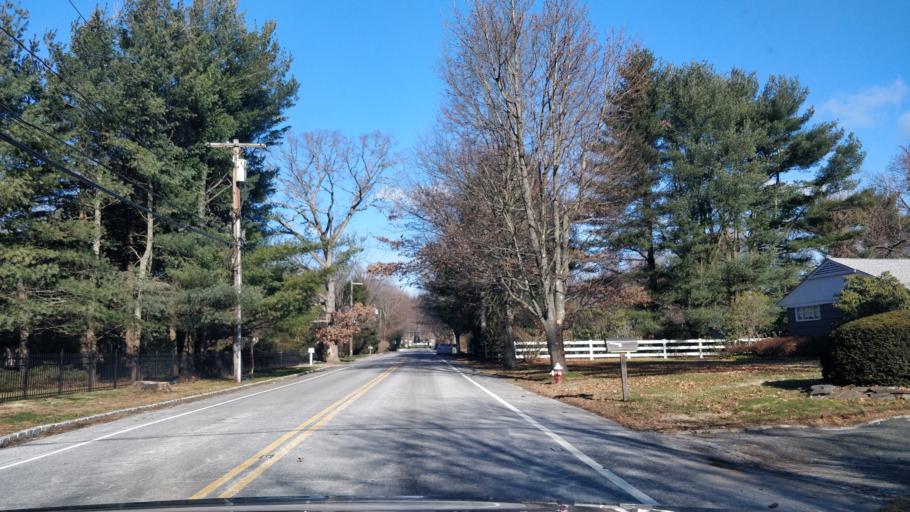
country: US
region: New York
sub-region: Nassau County
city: East Hills
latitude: 40.7891
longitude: -73.6148
